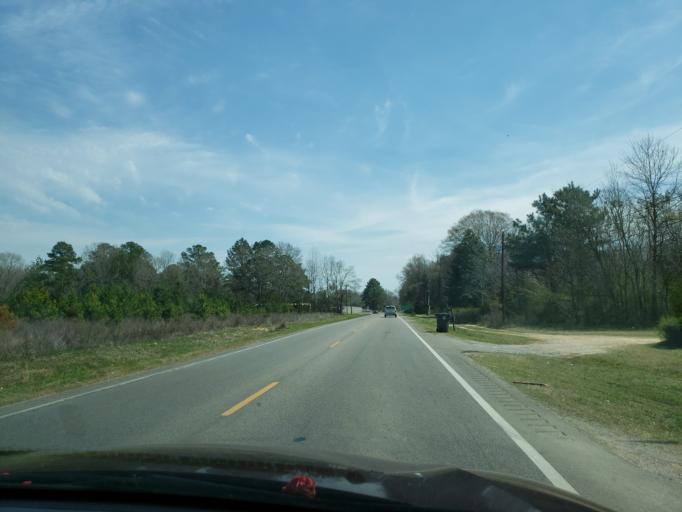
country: US
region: Alabama
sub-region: Autauga County
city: Prattville
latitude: 32.4310
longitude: -86.4927
